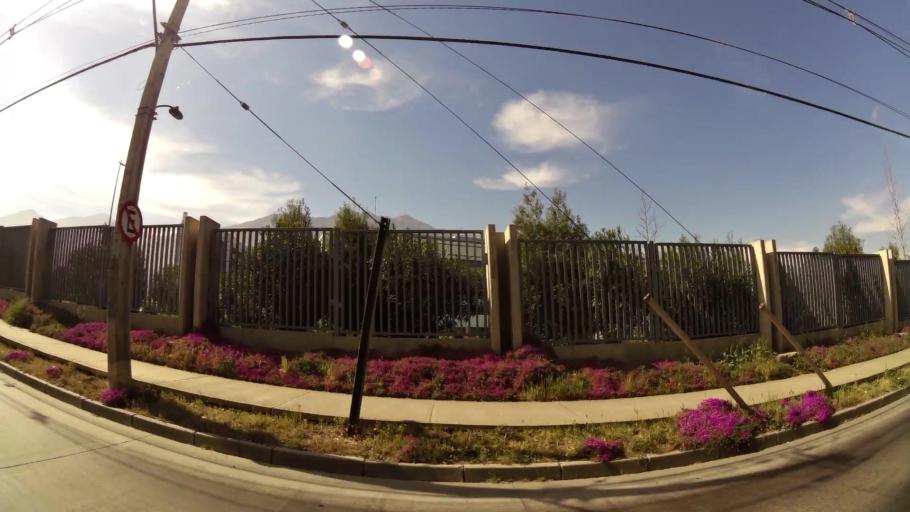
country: CL
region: Santiago Metropolitan
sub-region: Provincia de Santiago
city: Villa Presidente Frei, Nunoa, Santiago, Chile
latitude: -33.4497
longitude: -70.5398
